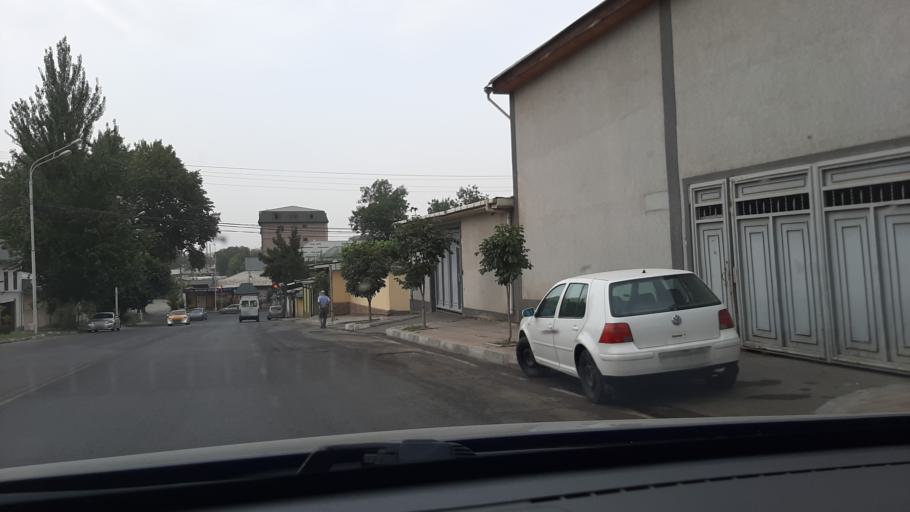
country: TJ
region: Dushanbe
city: Dushanbe
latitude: 38.6094
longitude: 68.7826
